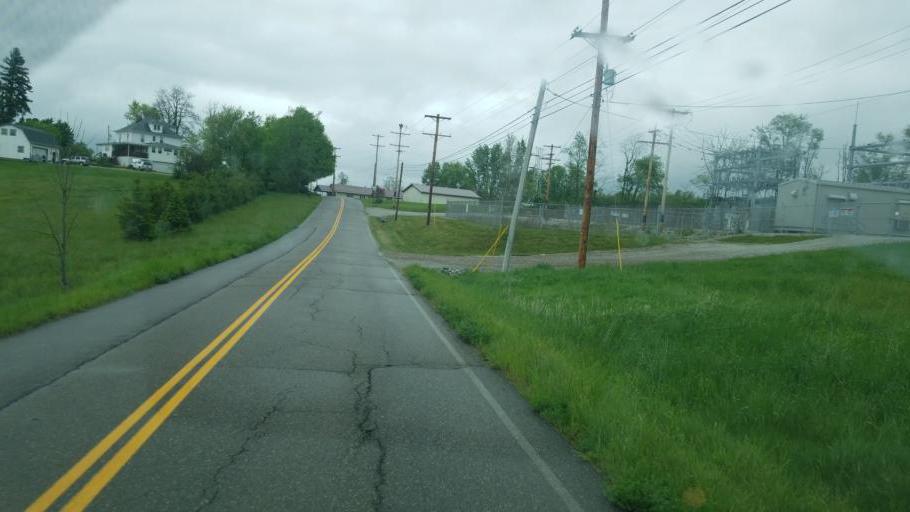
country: US
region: Ohio
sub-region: Jefferson County
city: Tiltonsville
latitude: 40.2539
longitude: -80.7522
